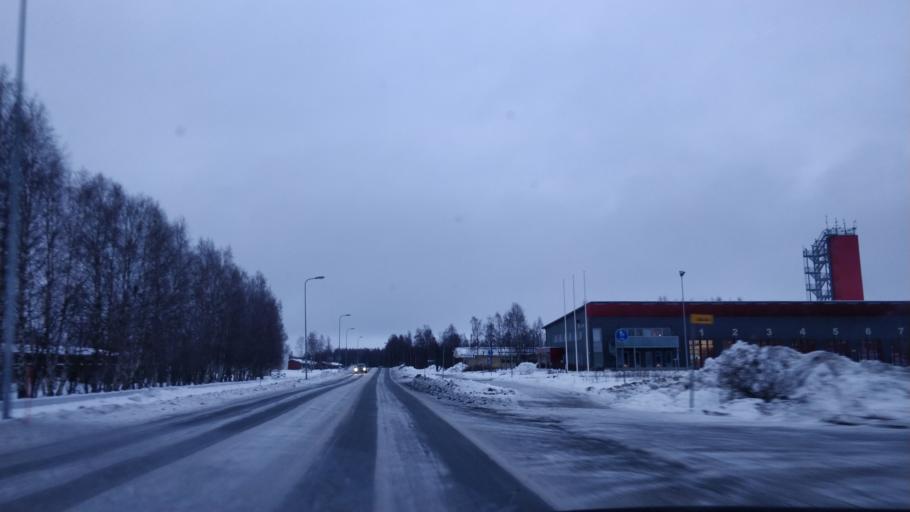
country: FI
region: Lapland
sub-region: Kemi-Tornio
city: Kemi
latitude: 65.7436
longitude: 24.5897
